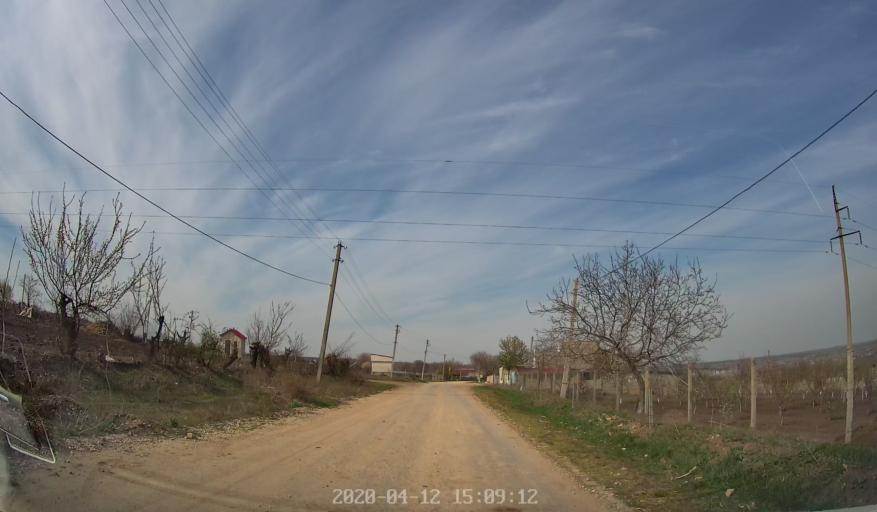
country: MD
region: Telenesti
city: Cocieri
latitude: 47.3192
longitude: 29.0691
